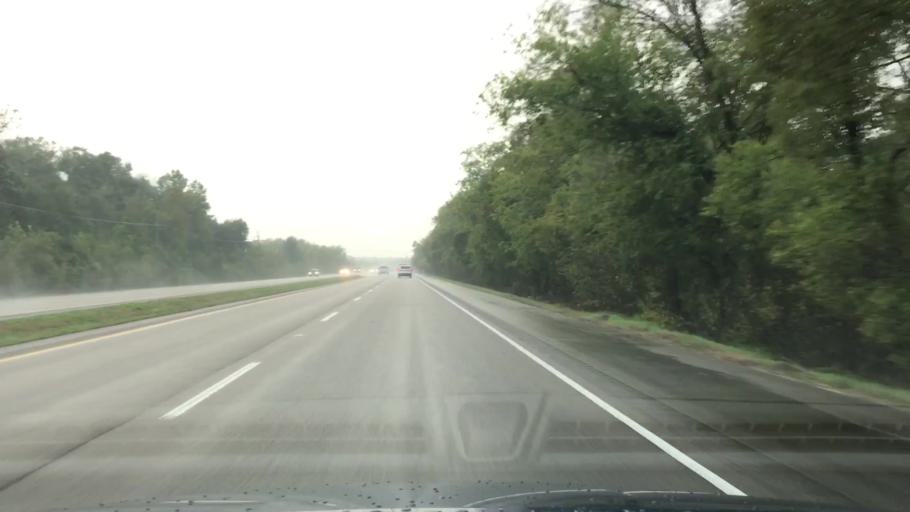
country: US
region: Louisiana
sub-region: Saint Charles Parish
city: Paradis
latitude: 29.8652
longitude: -90.4453
